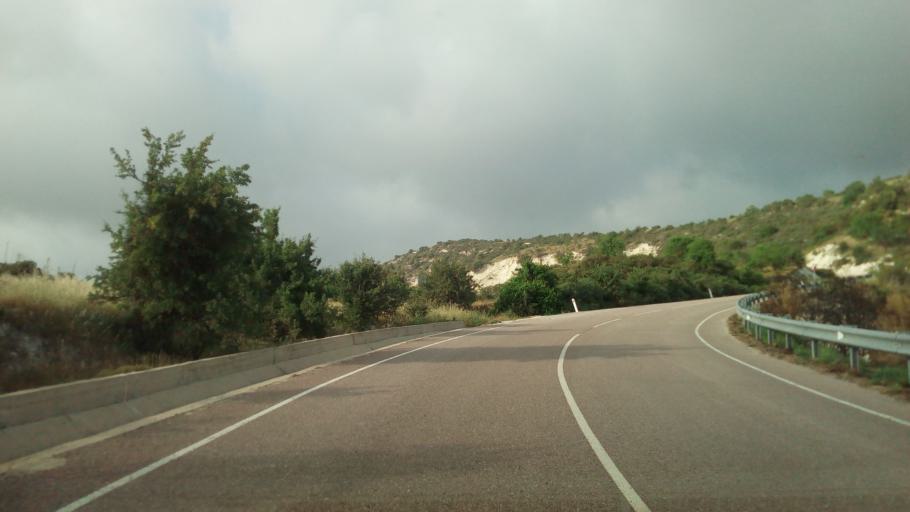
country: CY
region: Limassol
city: Pachna
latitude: 34.8253
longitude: 32.6841
